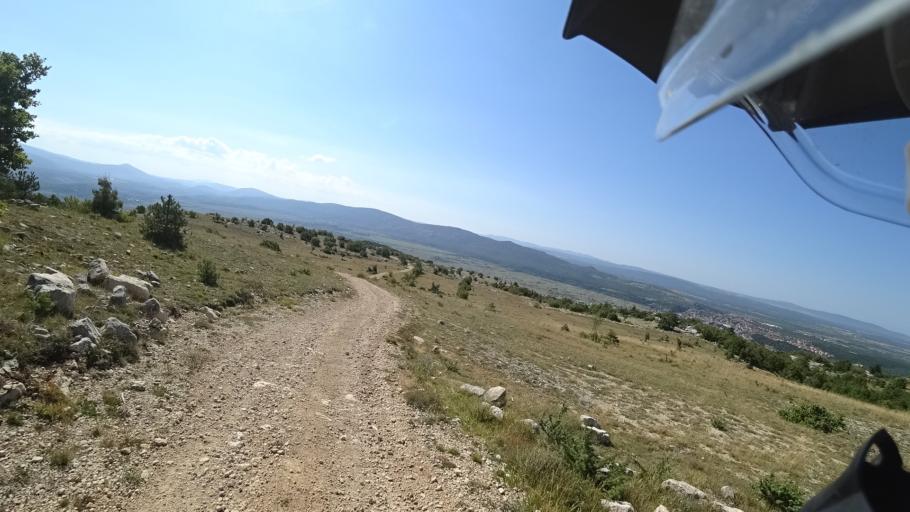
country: HR
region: Sibensko-Kniniska
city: Drnis
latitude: 43.8845
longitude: 16.1804
